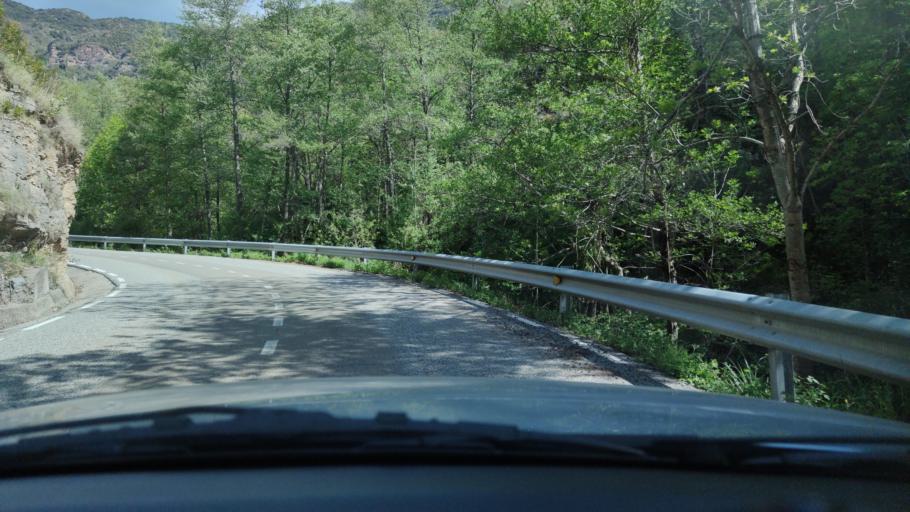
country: ES
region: Catalonia
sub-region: Provincia de Lleida
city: Coll de Nargo
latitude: 42.3114
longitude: 1.2895
